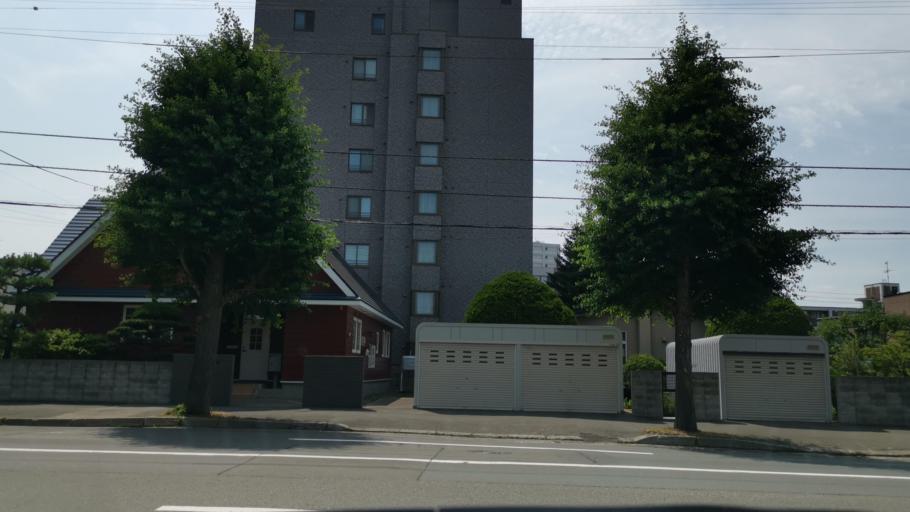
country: JP
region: Hokkaido
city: Sapporo
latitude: 43.0489
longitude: 141.3287
